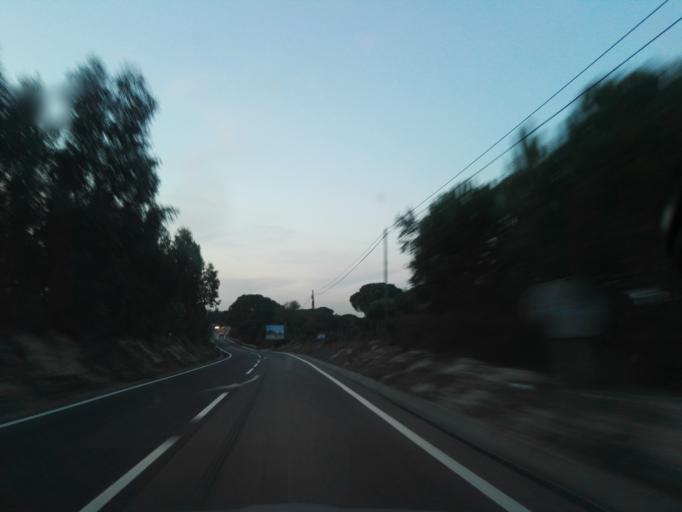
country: PT
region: Santarem
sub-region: Benavente
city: Benavente
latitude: 38.9335
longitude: -8.7810
